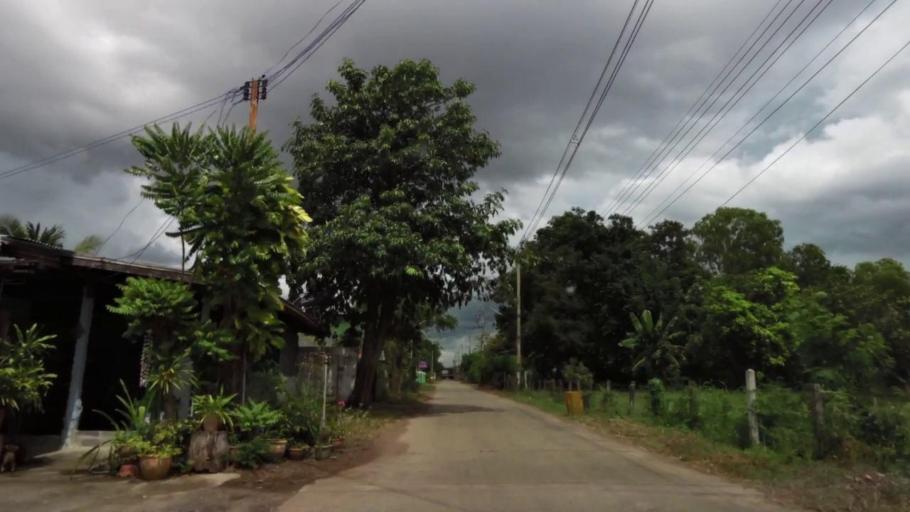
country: TH
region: Nakhon Sawan
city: Phai Sali
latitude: 15.5954
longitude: 100.6492
